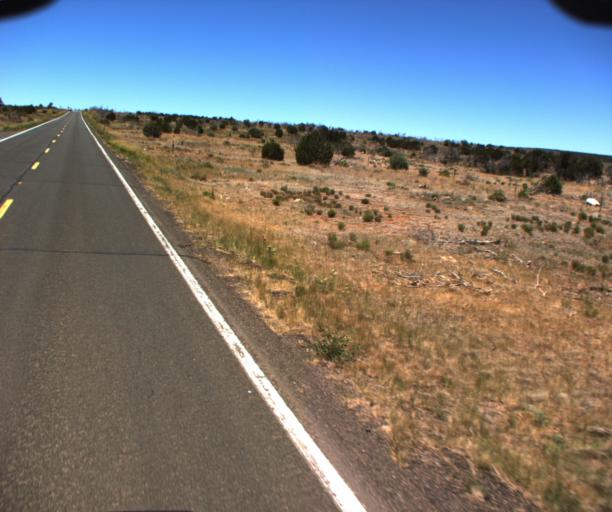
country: US
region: Arizona
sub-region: Coconino County
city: LeChee
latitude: 34.7279
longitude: -111.0812
